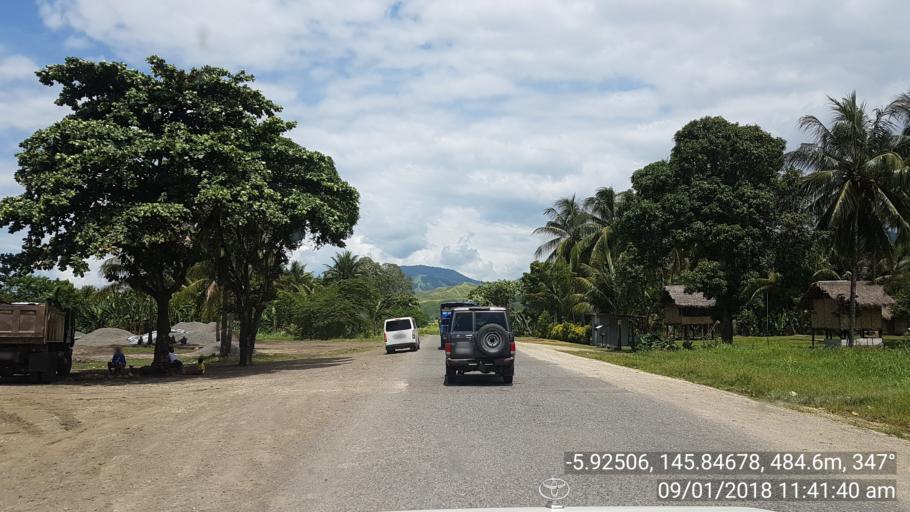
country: PG
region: Eastern Highlands
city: Kainantu
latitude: -5.9250
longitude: 145.8467
